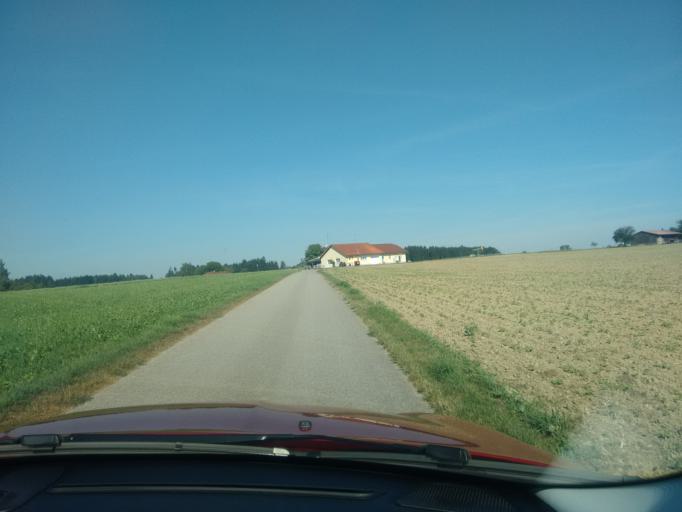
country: AT
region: Upper Austria
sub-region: Wels-Land
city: Sattledt
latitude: 48.0962
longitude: 14.0568
